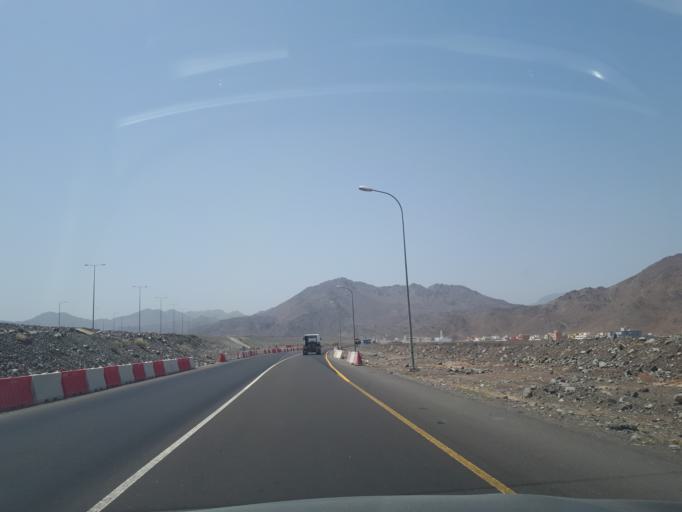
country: OM
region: Muhafazat ad Dakhiliyah
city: Sufalat Sama'il
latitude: 23.2699
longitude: 58.1045
